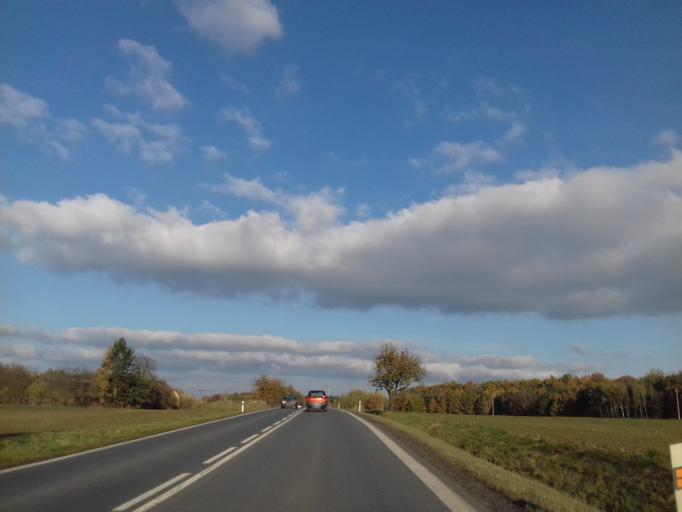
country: CZ
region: Plzensky
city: Chotesov
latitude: 49.6684
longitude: 13.2115
